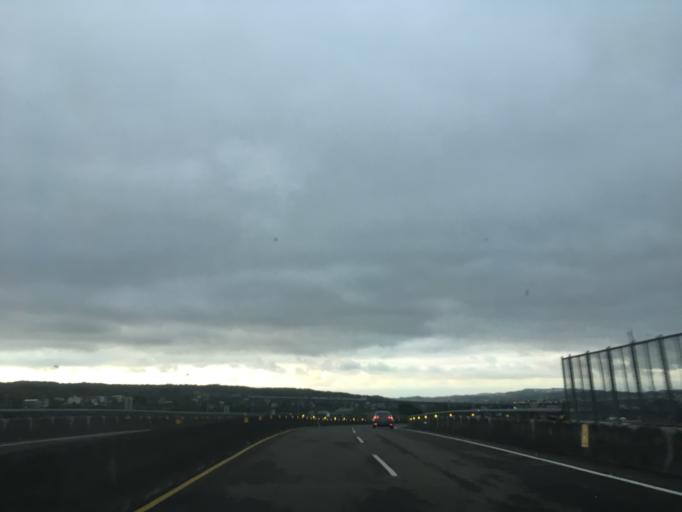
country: TW
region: Taiwan
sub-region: Miaoli
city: Miaoli
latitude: 24.4599
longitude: 120.7812
